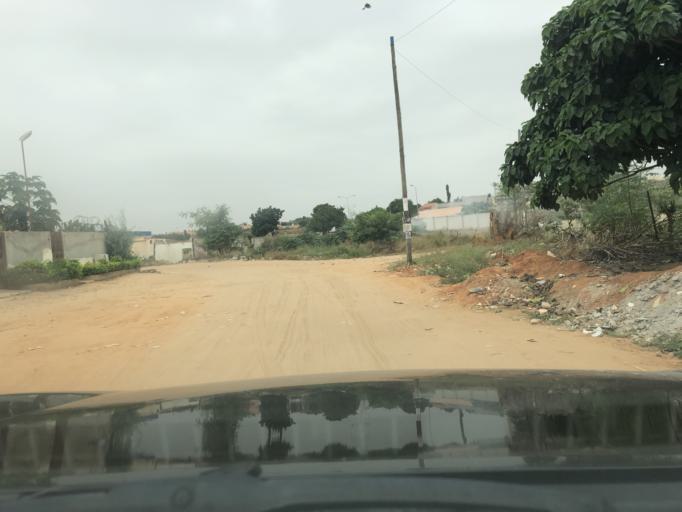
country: AO
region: Luanda
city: Luanda
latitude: -8.9377
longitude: 13.2447
